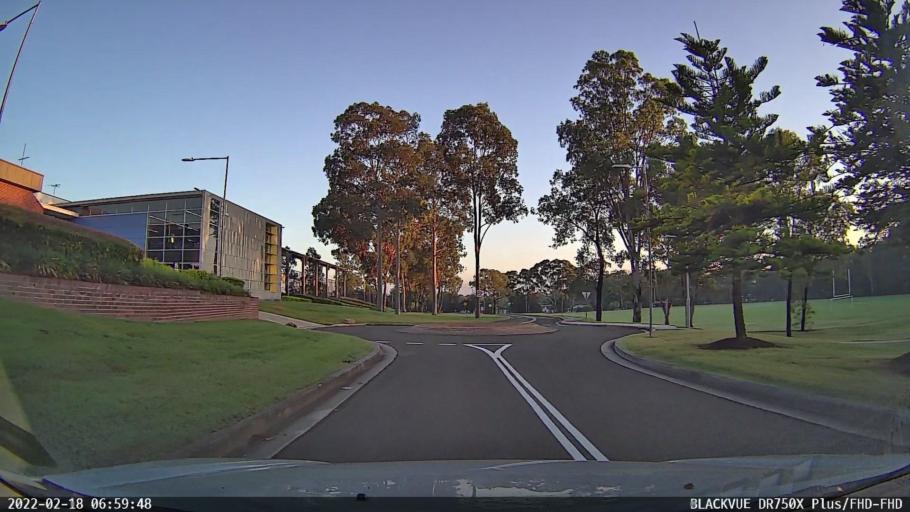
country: AU
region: New South Wales
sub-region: Penrith Municipality
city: Kingswood Park
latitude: -33.7667
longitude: 150.7304
